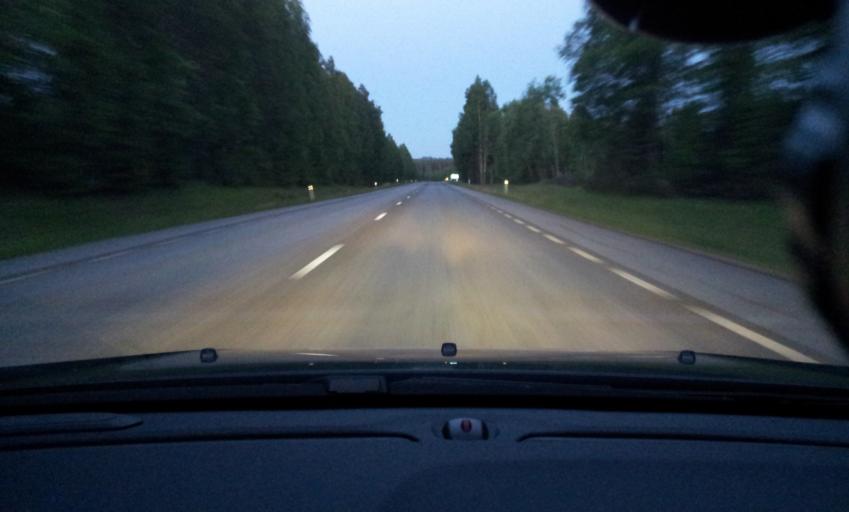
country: SE
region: Jaemtland
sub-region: Braecke Kommun
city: Braecke
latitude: 62.7222
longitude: 15.4482
